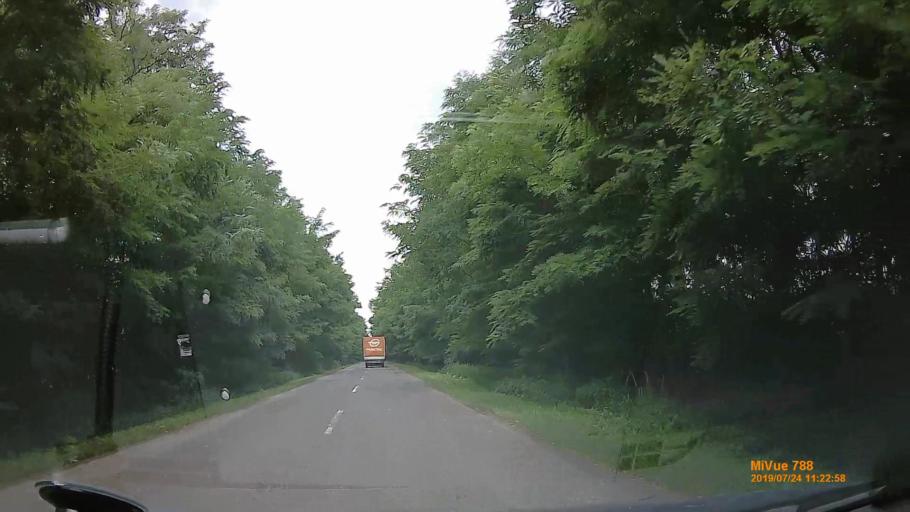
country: HU
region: Szabolcs-Szatmar-Bereg
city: Tarpa
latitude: 48.1839
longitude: 22.4634
